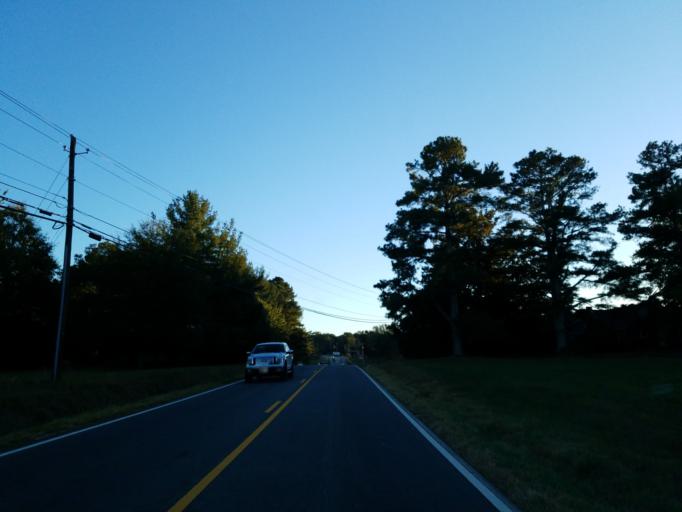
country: US
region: Georgia
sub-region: Forsyth County
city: Cumming
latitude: 34.2658
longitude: -84.1034
